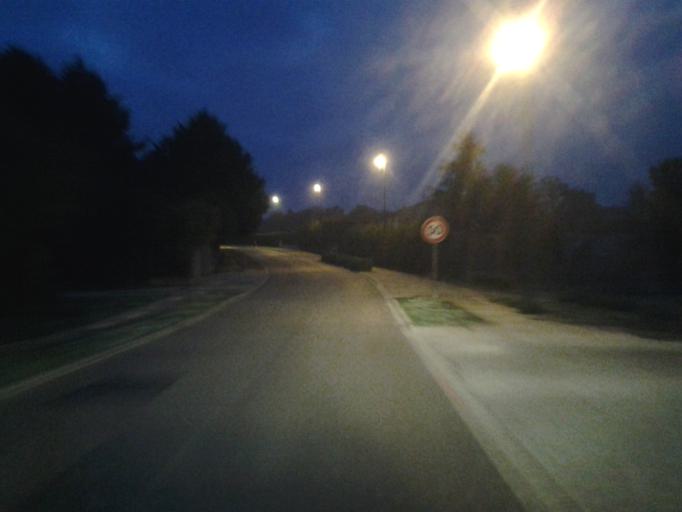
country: FR
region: Pays de la Loire
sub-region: Departement de la Vendee
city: Landeronde
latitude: 46.6553
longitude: -1.5649
